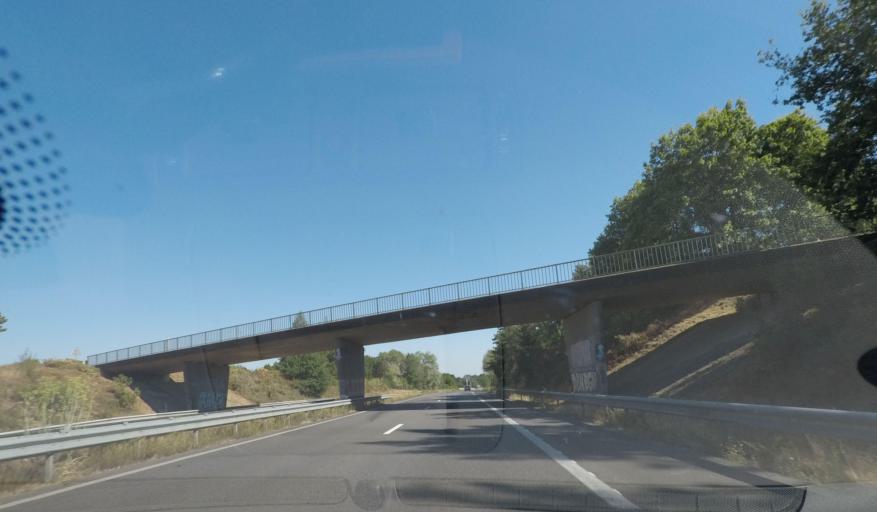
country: FR
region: Pays de la Loire
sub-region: Departement de la Loire-Atlantique
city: Missillac
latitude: 47.4776
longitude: -2.1816
